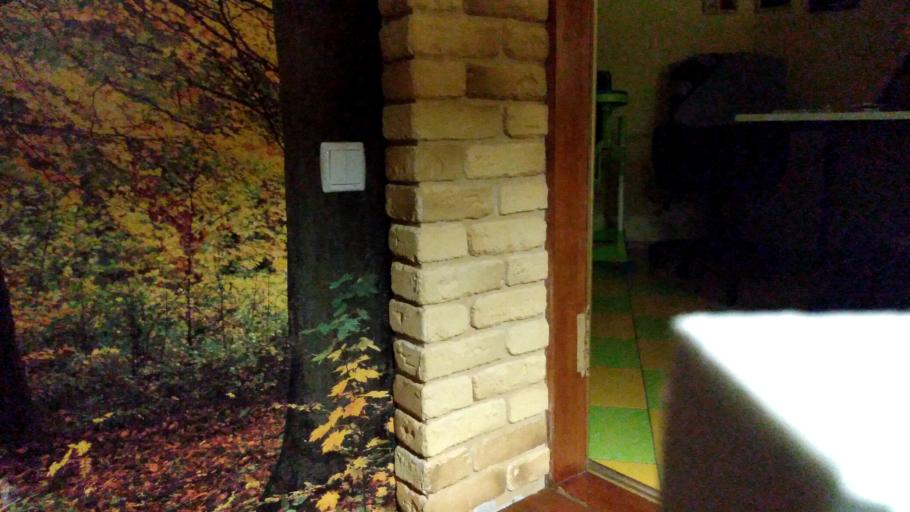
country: RU
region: Vologda
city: Lipin Bor
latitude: 61.1127
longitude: 37.9202
